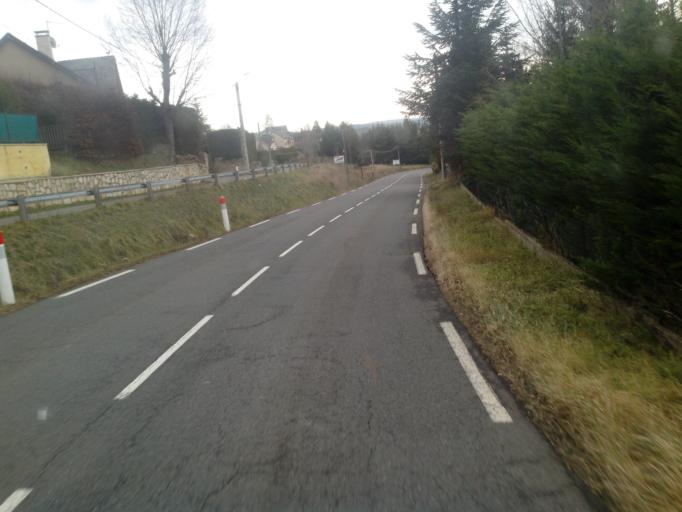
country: FR
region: Languedoc-Roussillon
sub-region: Departement de la Lozere
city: Mende
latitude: 44.5614
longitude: 3.5042
